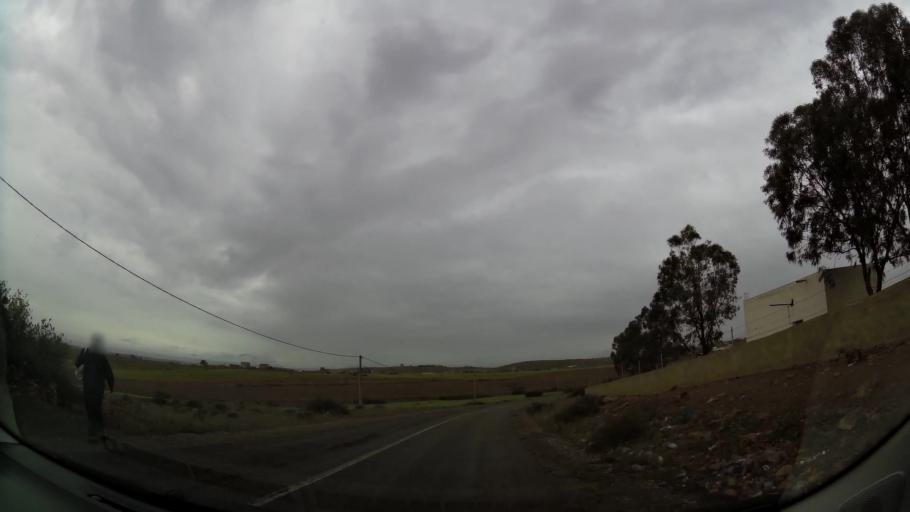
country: MA
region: Oriental
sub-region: Nador
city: Tiztoutine
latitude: 35.0609
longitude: -3.2341
